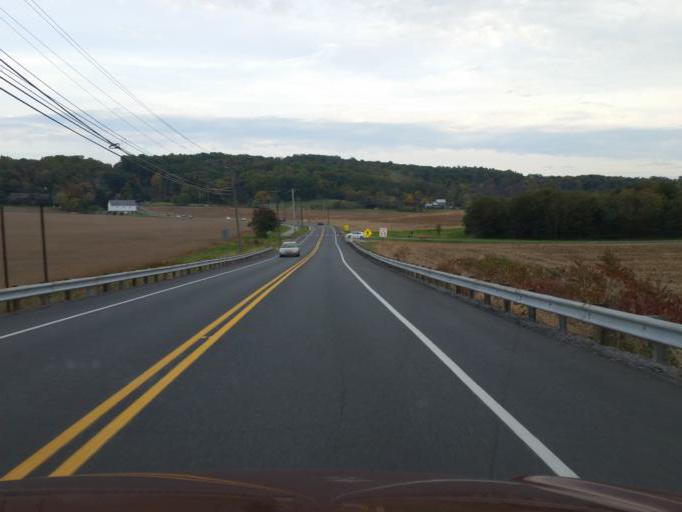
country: US
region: Pennsylvania
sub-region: Dauphin County
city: Hummelstown
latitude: 40.2579
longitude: -76.6993
